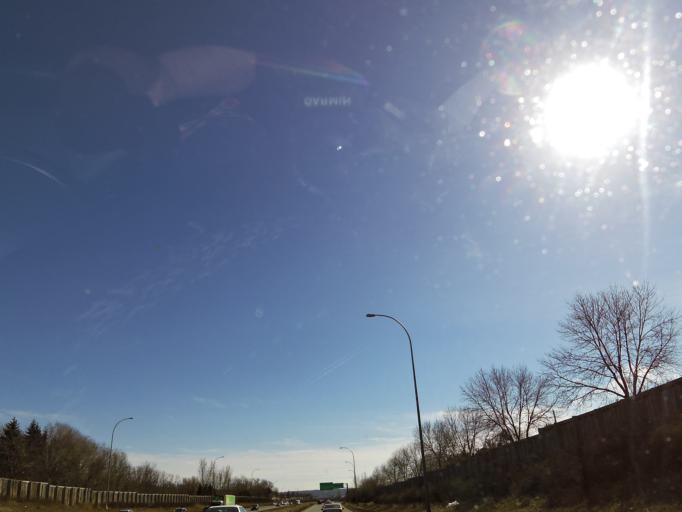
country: US
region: Minnesota
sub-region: Scott County
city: Savage
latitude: 44.8253
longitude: -93.3985
